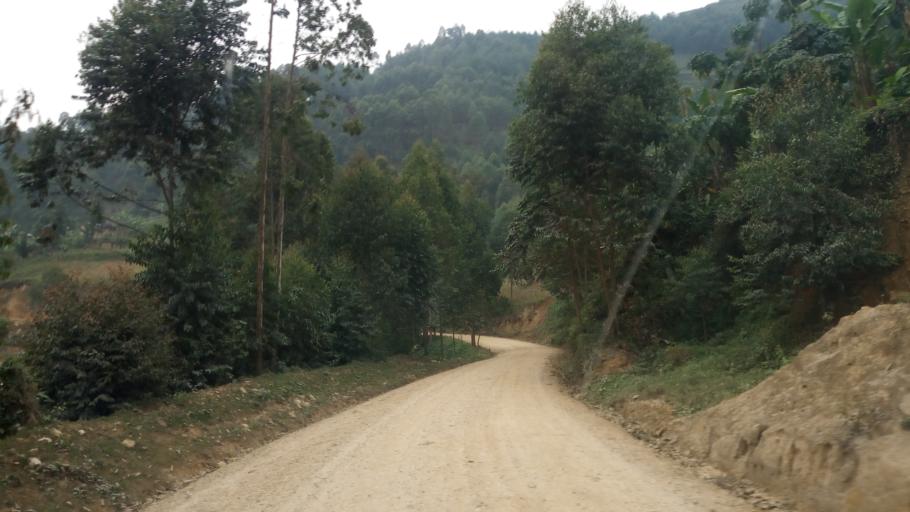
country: UG
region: Western Region
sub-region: Kanungu District
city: Kanungu
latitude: -1.0986
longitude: 29.8512
